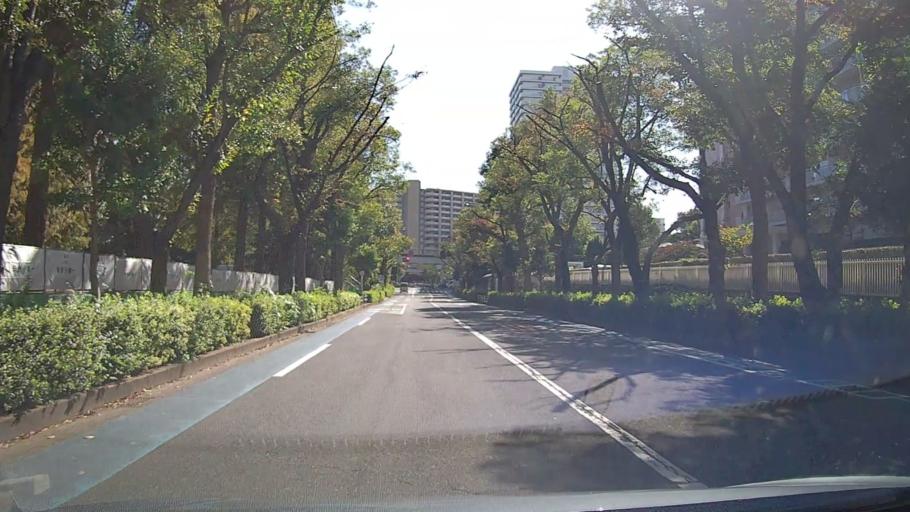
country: JP
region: Saitama
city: Wako
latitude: 35.7600
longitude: 139.6254
